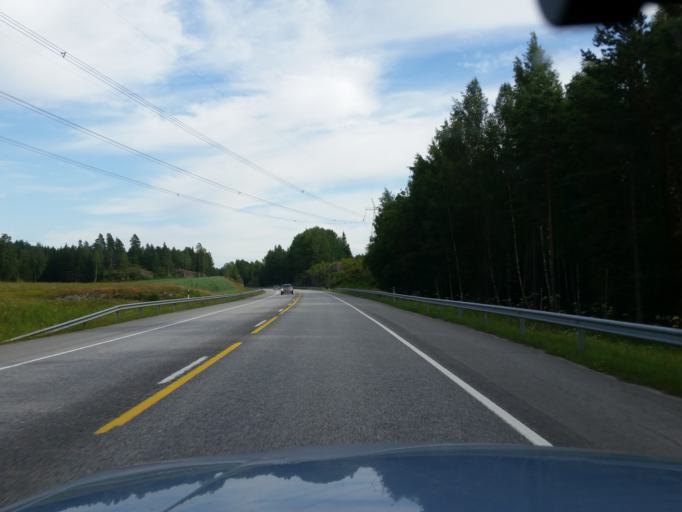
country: FI
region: Uusimaa
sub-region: Raaseporin
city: Karis
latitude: 60.0702
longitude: 23.7809
